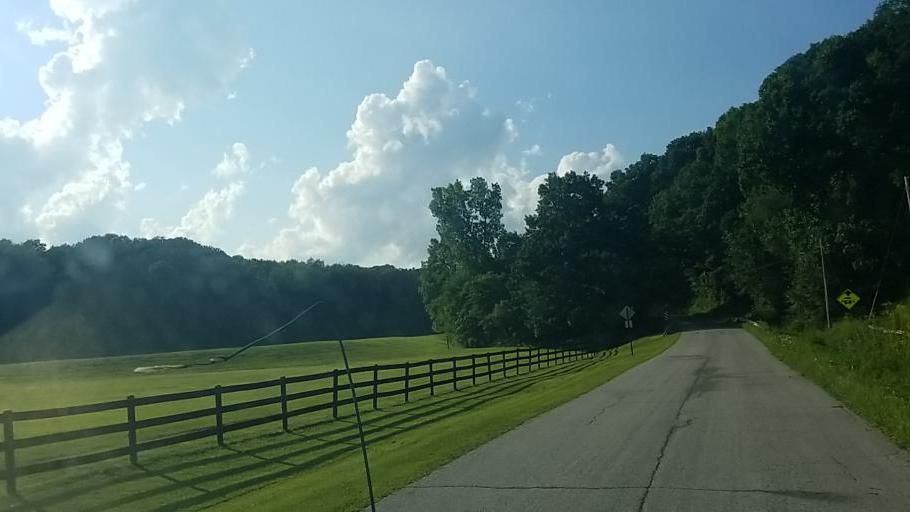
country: US
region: Ohio
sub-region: Wayne County
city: Wooster
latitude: 40.8748
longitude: -82.0277
